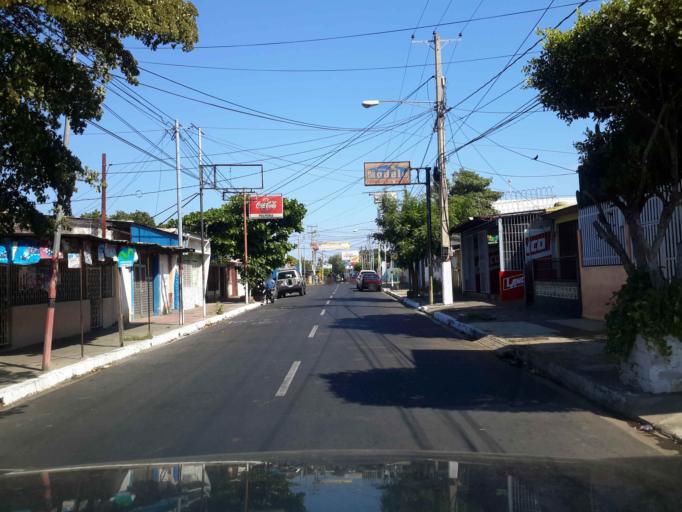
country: NI
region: Managua
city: Managua
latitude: 12.1490
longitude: -86.2939
